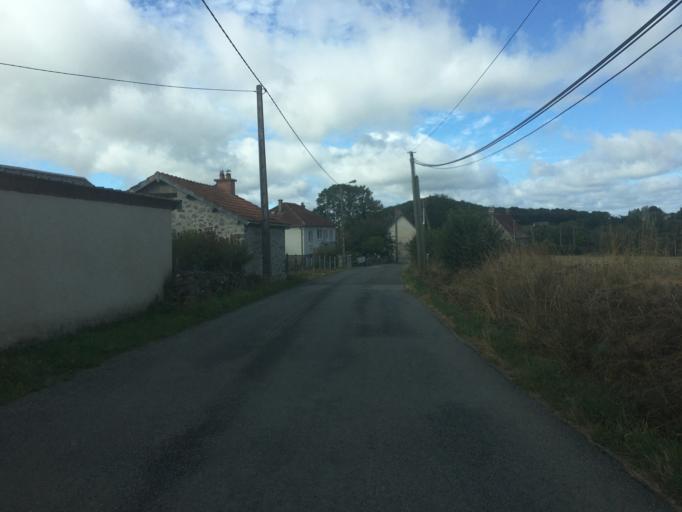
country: FR
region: Limousin
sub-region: Departement de la Correze
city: Bort-les-Orgues
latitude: 45.4135
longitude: 2.4357
